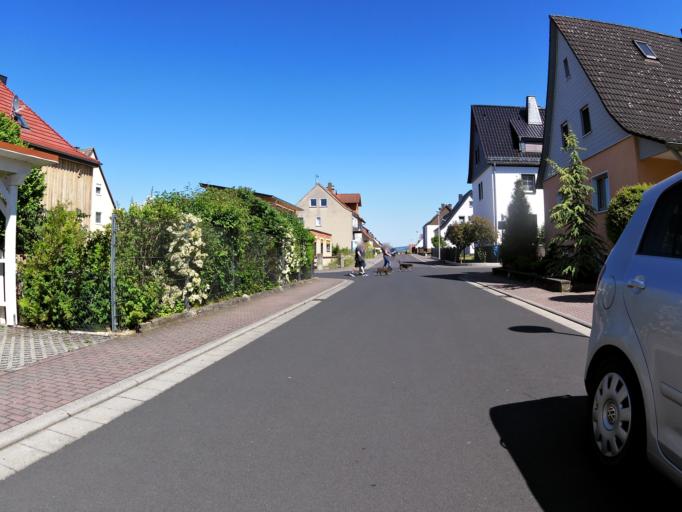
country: DE
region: Thuringia
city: Dankmarshausen
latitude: 50.9465
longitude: 10.0319
